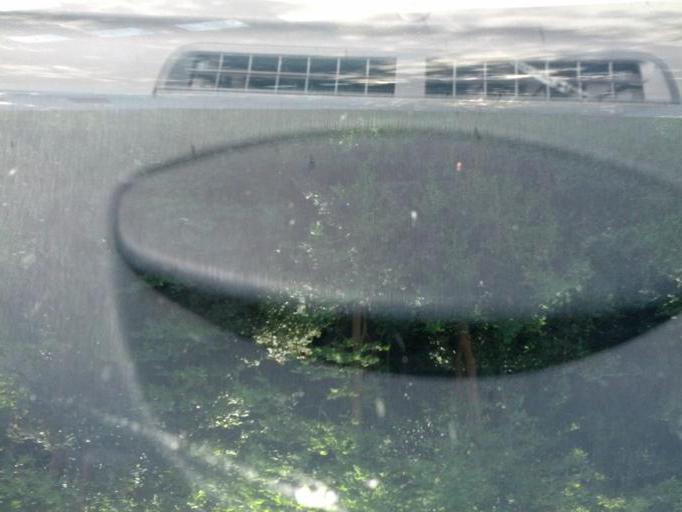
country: SI
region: Ljubljana
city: Ljubljana
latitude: 46.0411
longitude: 14.5154
